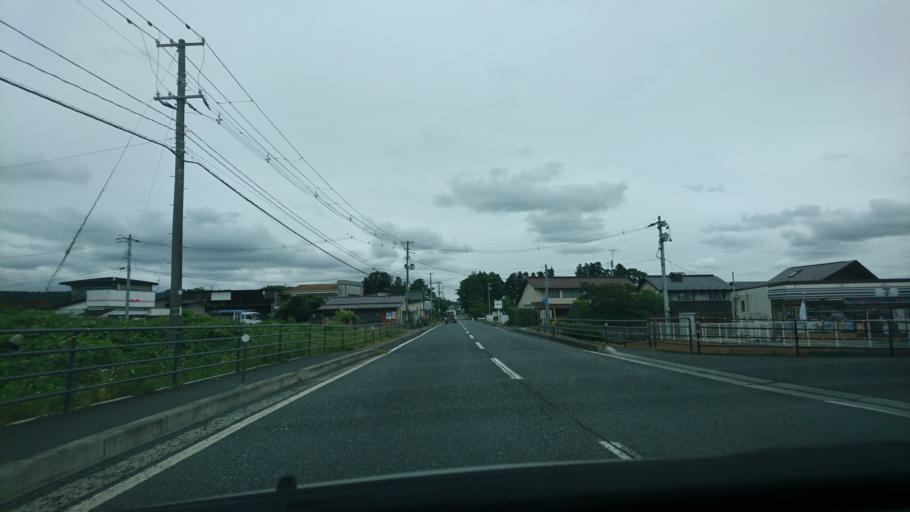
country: JP
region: Iwate
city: Ichinoseki
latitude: 38.9738
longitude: 141.1177
